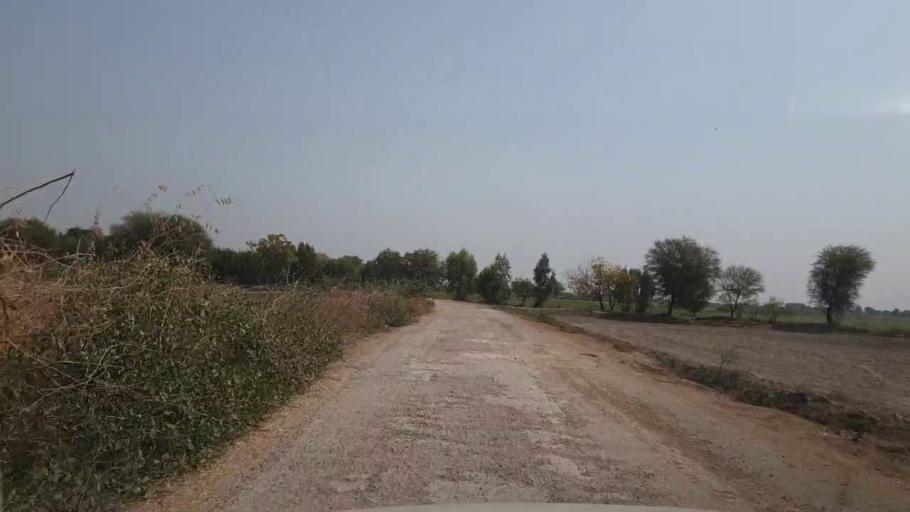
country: PK
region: Sindh
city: Dhoro Naro
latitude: 25.4684
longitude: 69.6384
